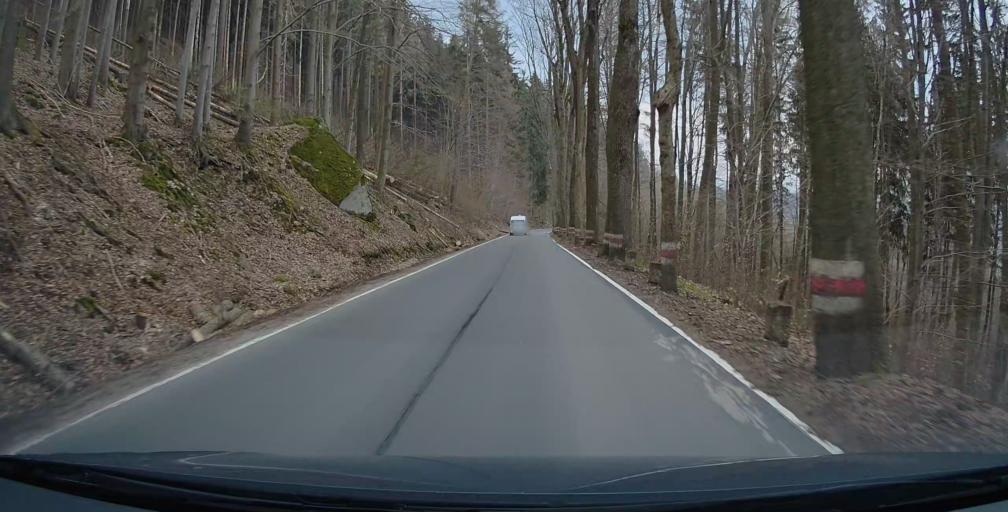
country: PL
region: Lower Silesian Voivodeship
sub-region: Powiat klodzki
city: Radkow
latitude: 50.4858
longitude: 16.3739
